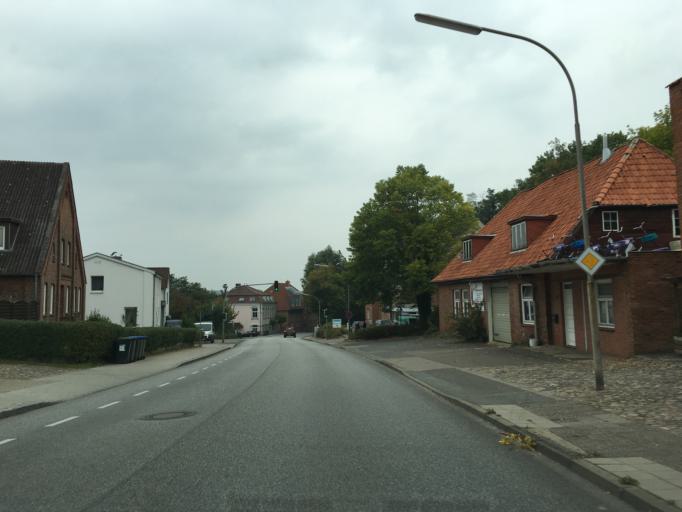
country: DE
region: Schleswig-Holstein
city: Ratzeburg
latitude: 53.6945
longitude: 10.7854
